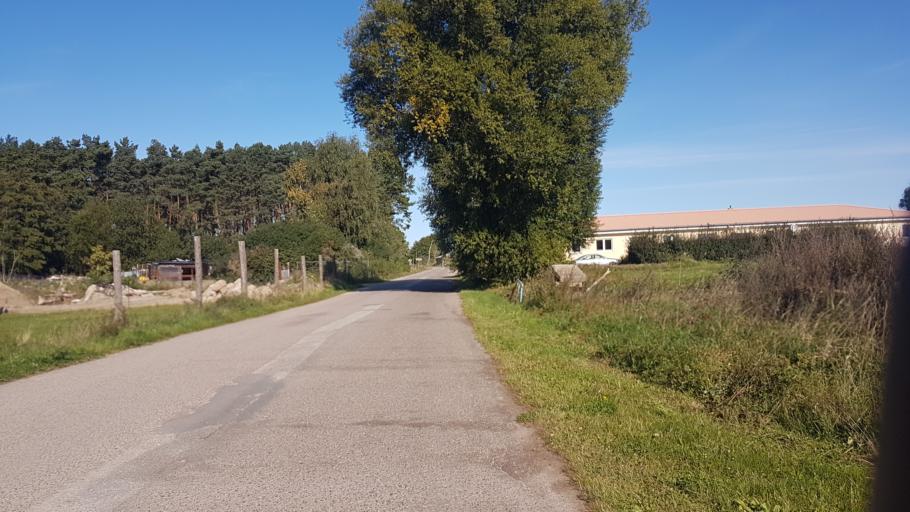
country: DE
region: Mecklenburg-Vorpommern
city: Sagard
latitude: 54.5225
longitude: 13.5178
